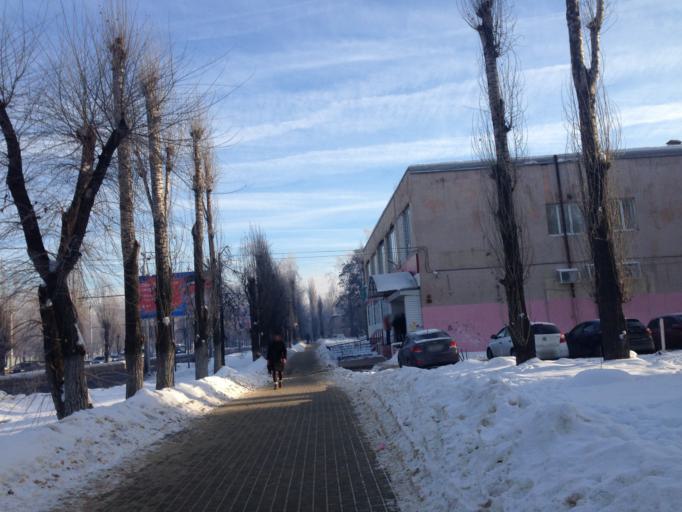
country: RU
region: Voronezj
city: Voronezh
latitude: 51.6582
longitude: 39.1464
